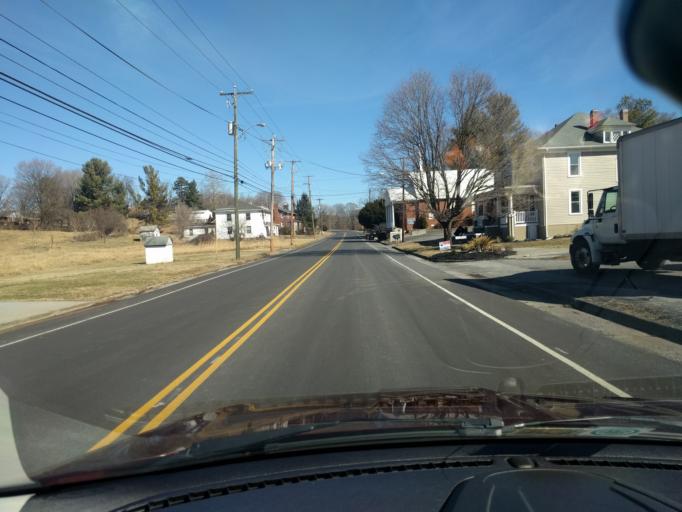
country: US
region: Virginia
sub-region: Botetourt County
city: Laymantown
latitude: 37.3221
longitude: -79.8703
